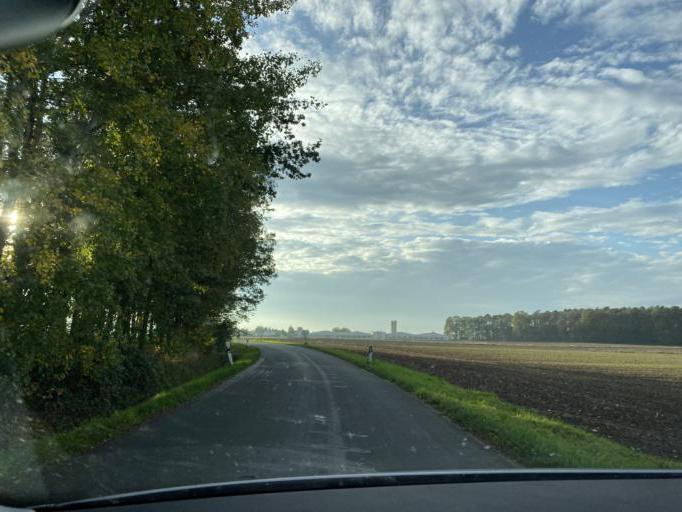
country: DE
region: Bavaria
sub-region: Regierungsbezirk Mittelfranken
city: Puschendorf
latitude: 49.5361
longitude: 10.8052
